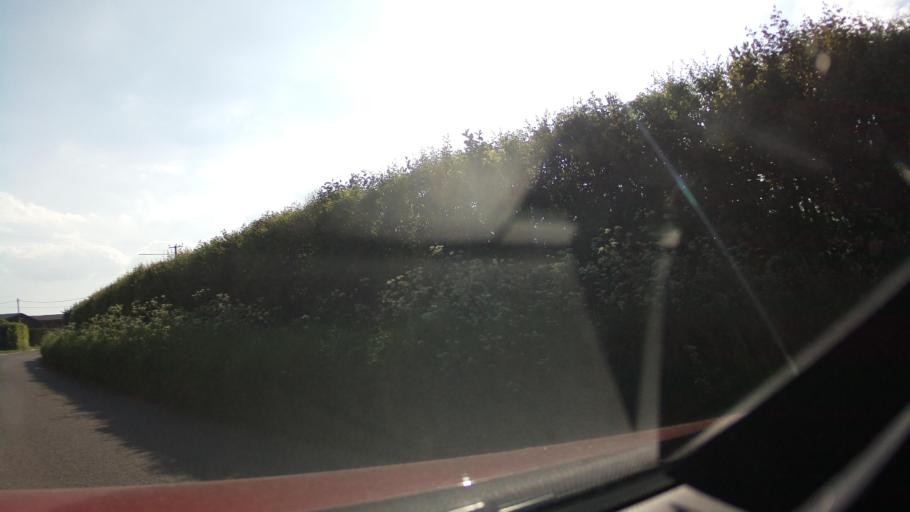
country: GB
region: England
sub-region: Wiltshire
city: Biddestone
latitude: 51.4818
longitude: -2.1703
